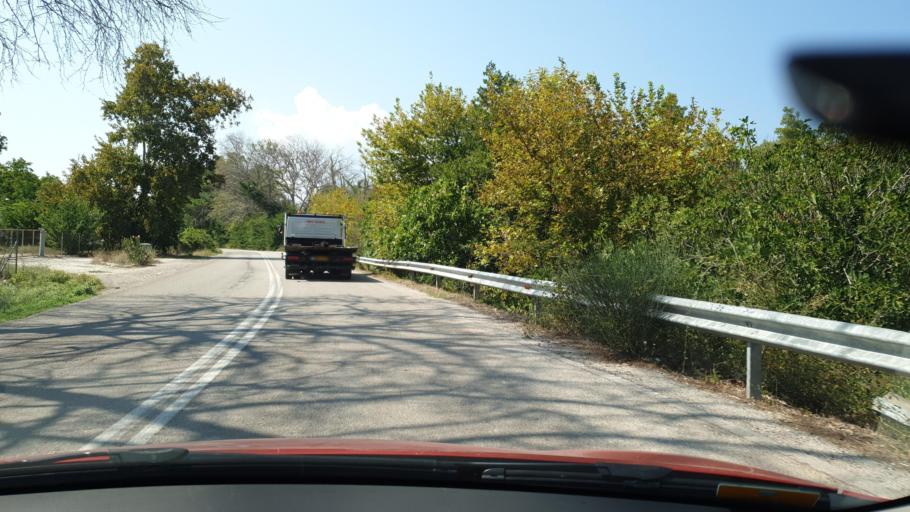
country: GR
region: Central Greece
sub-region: Nomos Evvoias
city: Prokopion
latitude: 38.7204
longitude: 23.5156
